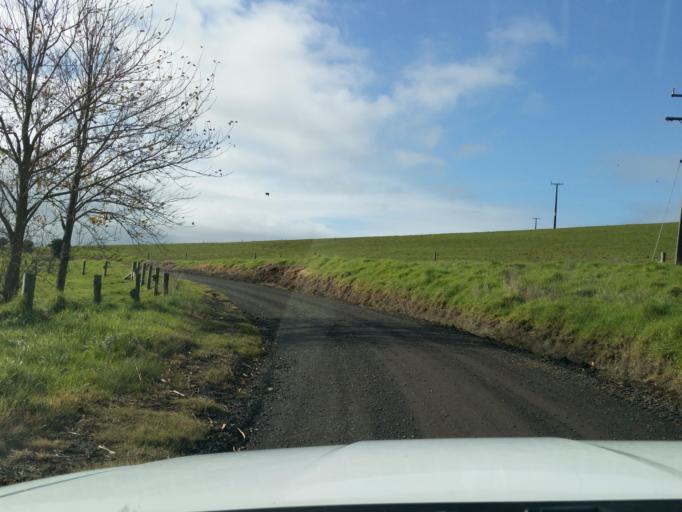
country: NZ
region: Northland
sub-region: Kaipara District
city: Dargaville
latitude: -35.7503
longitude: 173.5917
